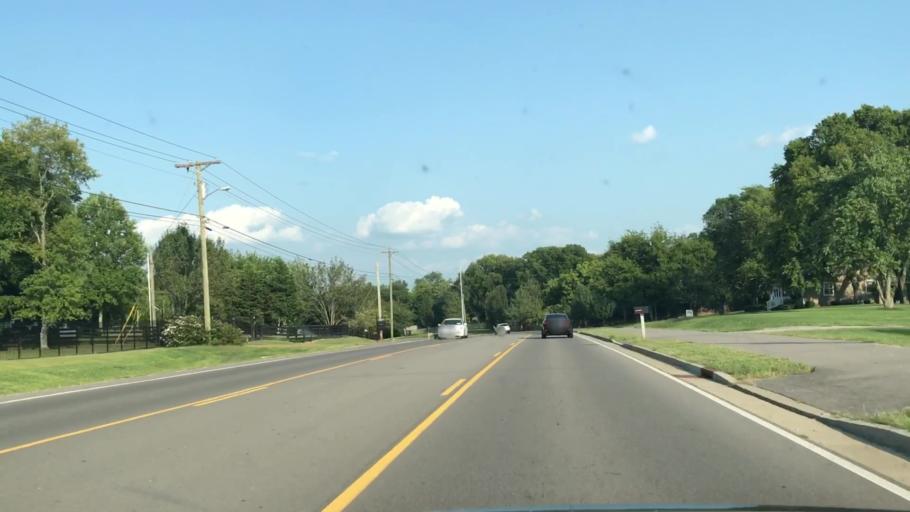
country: US
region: Tennessee
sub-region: Williamson County
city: Nolensville
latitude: 35.9835
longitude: -86.7207
